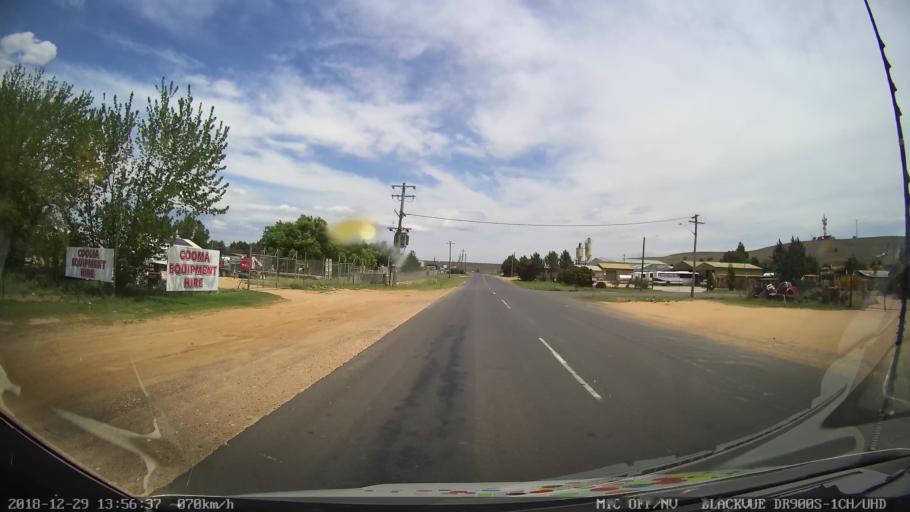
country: AU
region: New South Wales
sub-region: Cooma-Monaro
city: Cooma
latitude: -36.2323
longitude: 149.1458
